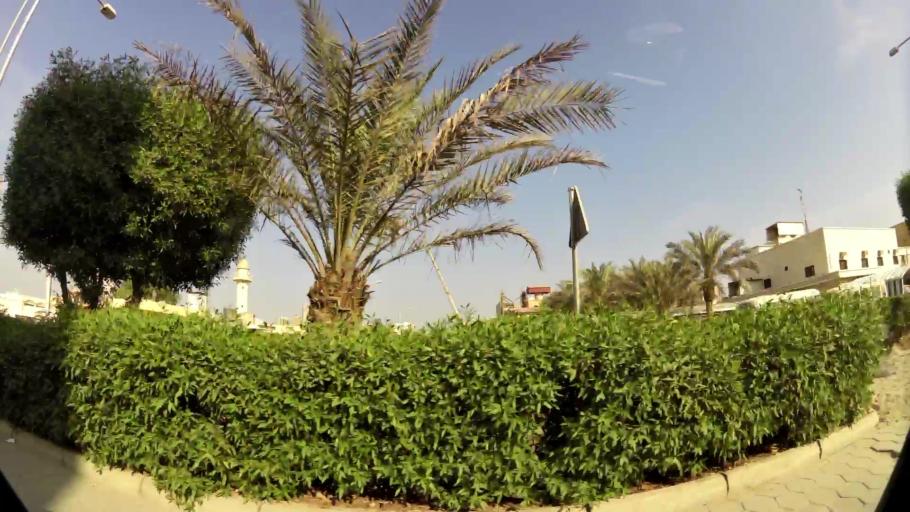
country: KW
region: Al Ahmadi
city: Ar Riqqah
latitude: 29.1543
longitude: 48.1044
